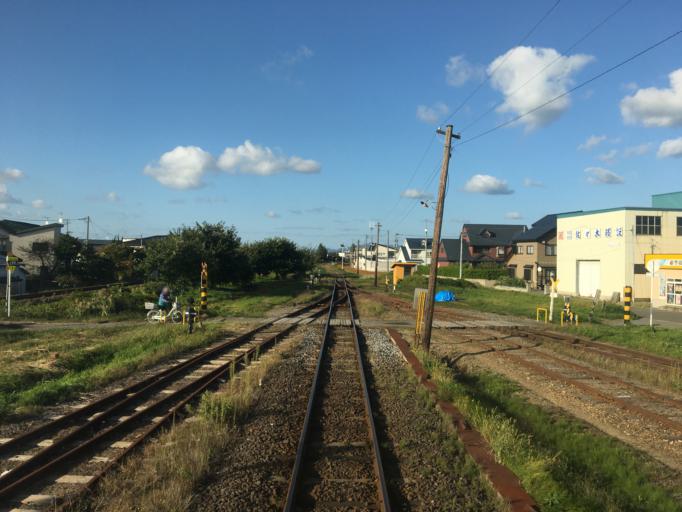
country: JP
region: Aomori
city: Goshogawara
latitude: 40.8108
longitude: 140.4488
